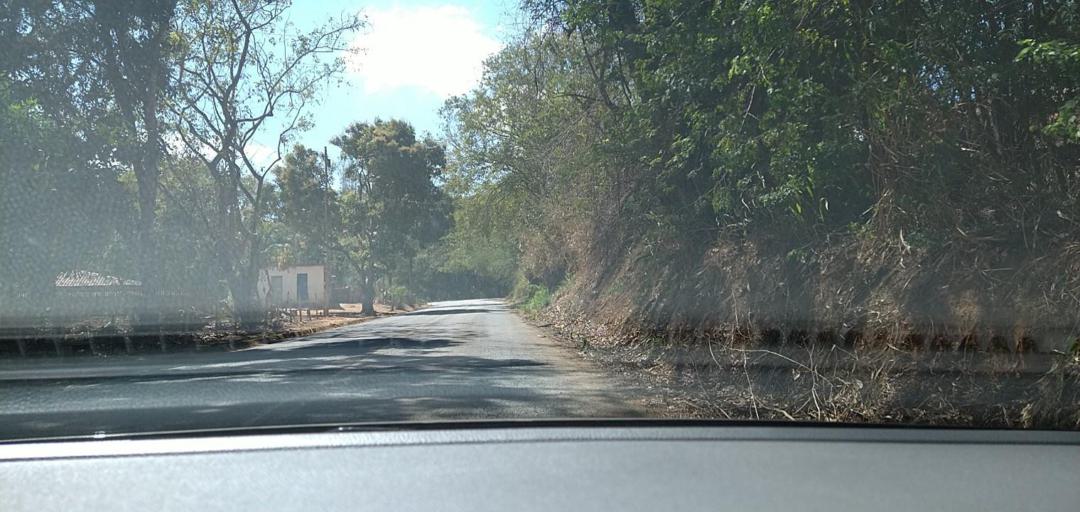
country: BR
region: Minas Gerais
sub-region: Ponte Nova
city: Ponte Nova
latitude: -20.2788
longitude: -42.9028
